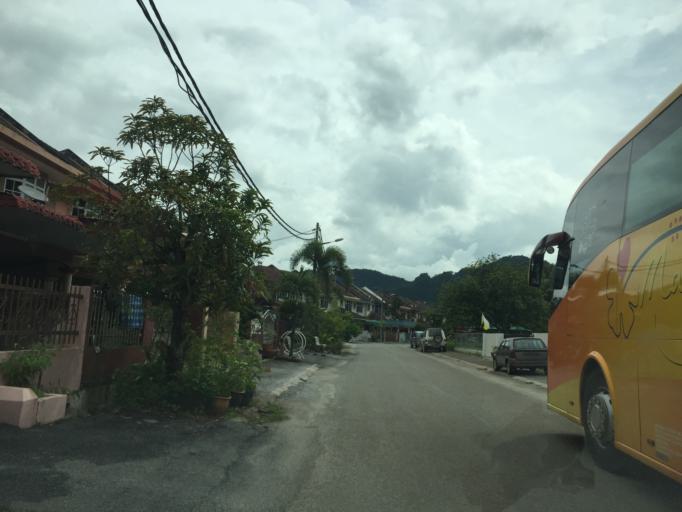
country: MY
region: Perak
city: Ipoh
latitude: 4.5665
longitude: 101.1193
